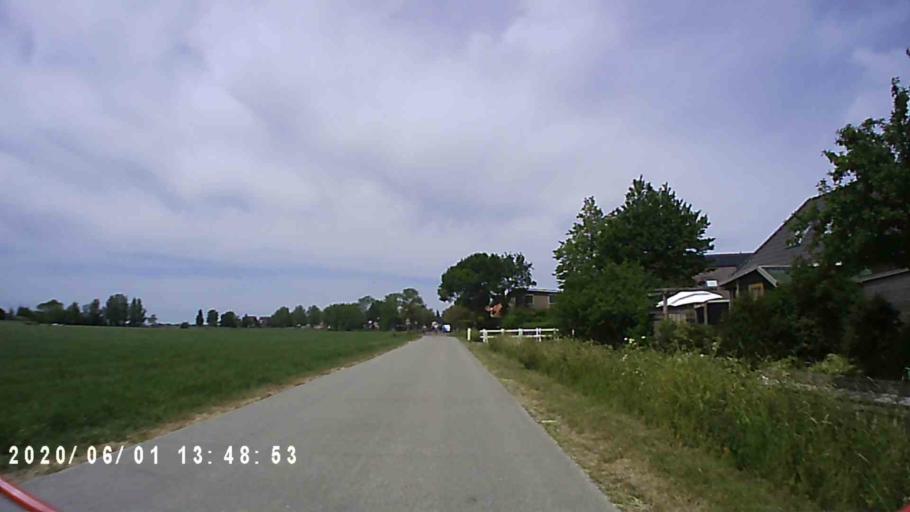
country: NL
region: Friesland
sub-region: Gemeente Littenseradiel
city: Wommels
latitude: 53.0940
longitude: 5.6190
